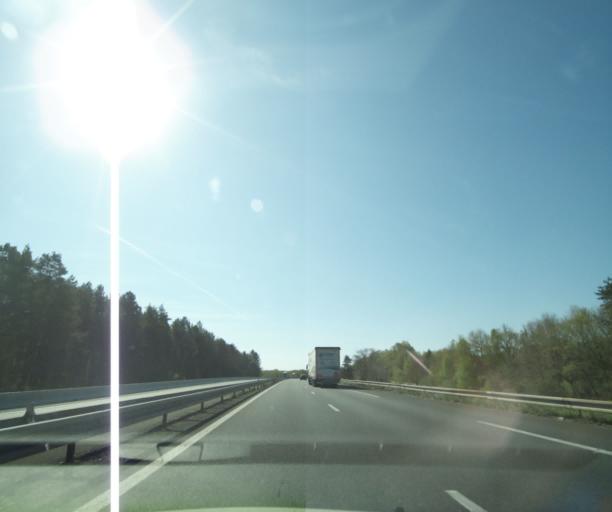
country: FR
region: Centre
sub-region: Departement du Loir-et-Cher
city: Nouan-le-Fuzelier
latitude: 47.5191
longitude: 2.0067
